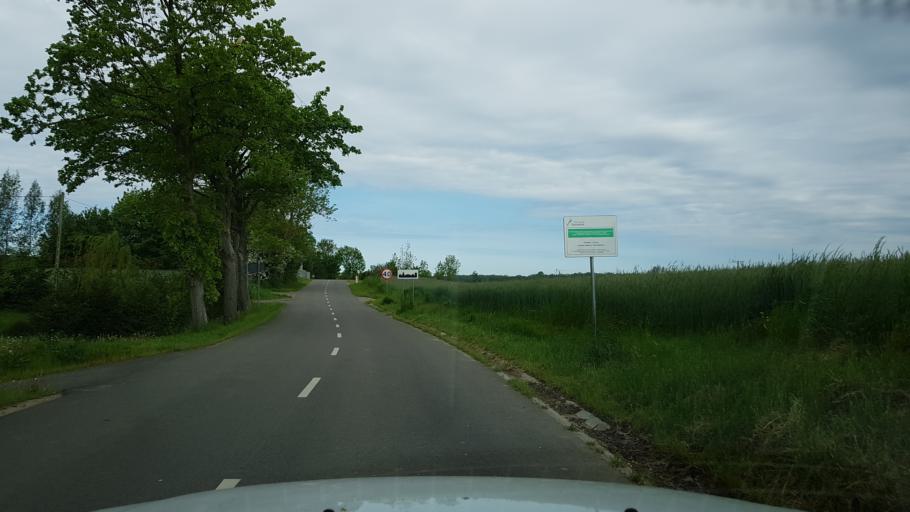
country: PL
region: West Pomeranian Voivodeship
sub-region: Powiat kolobrzeski
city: Ustronie Morskie
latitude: 54.2057
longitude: 15.8329
